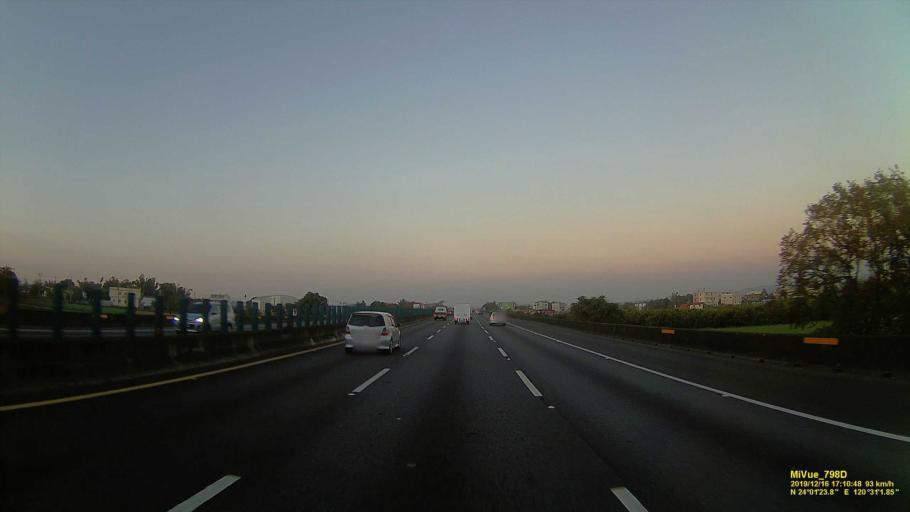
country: TW
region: Taiwan
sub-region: Changhua
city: Chang-hua
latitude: 24.0237
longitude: 120.5174
